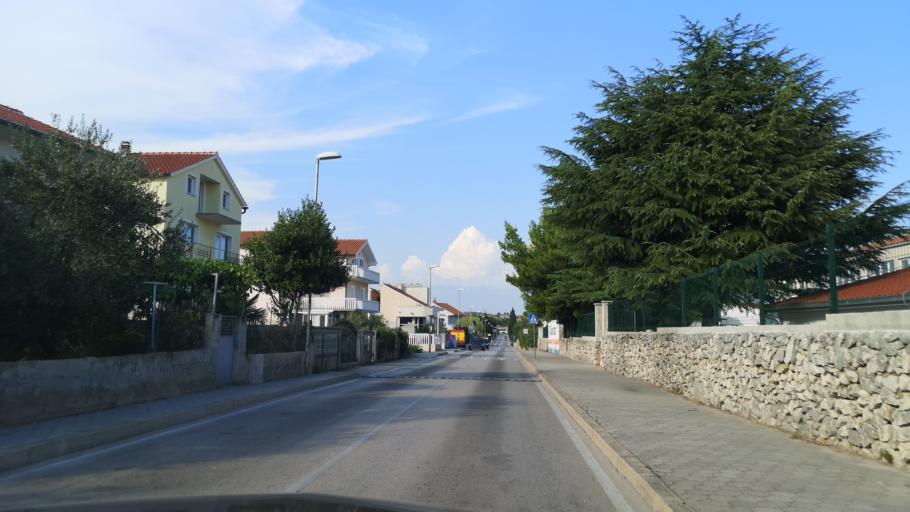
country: HR
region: Sibensko-Kniniska
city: Vodice
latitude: 43.7608
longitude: 15.7707
